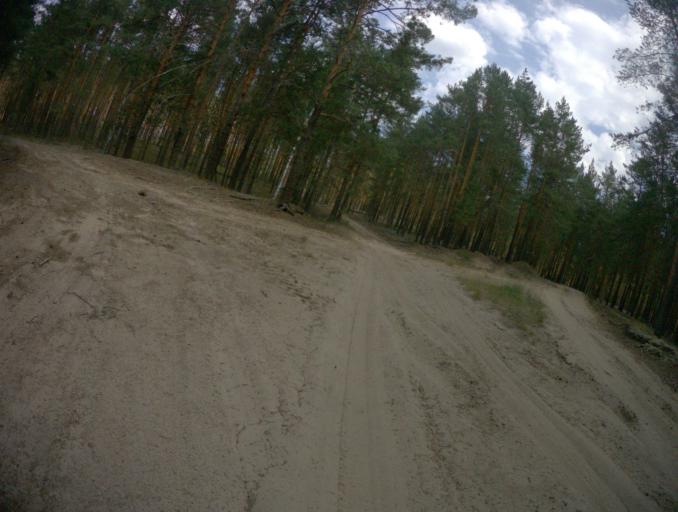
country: RU
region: Ivanovo
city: Talitsy
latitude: 56.3891
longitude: 42.3463
